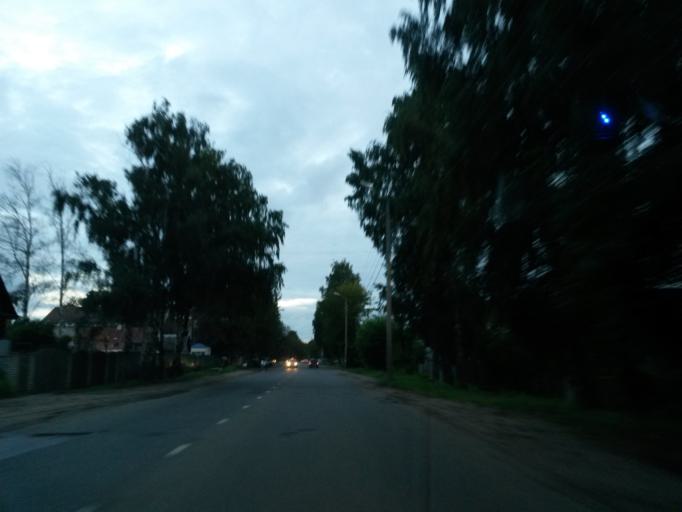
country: RU
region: Jaroslavl
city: Yaroslavl
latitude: 57.6499
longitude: 39.9067
